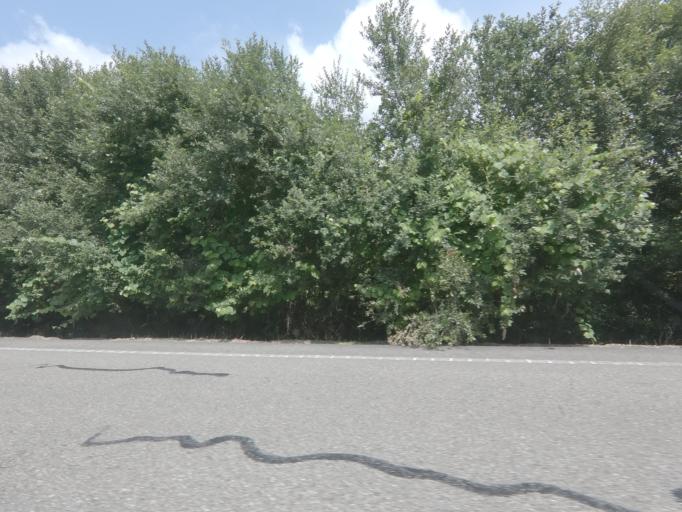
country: ES
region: Galicia
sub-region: Provincia de Pontevedra
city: Tomino
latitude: 42.0290
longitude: -8.7328
